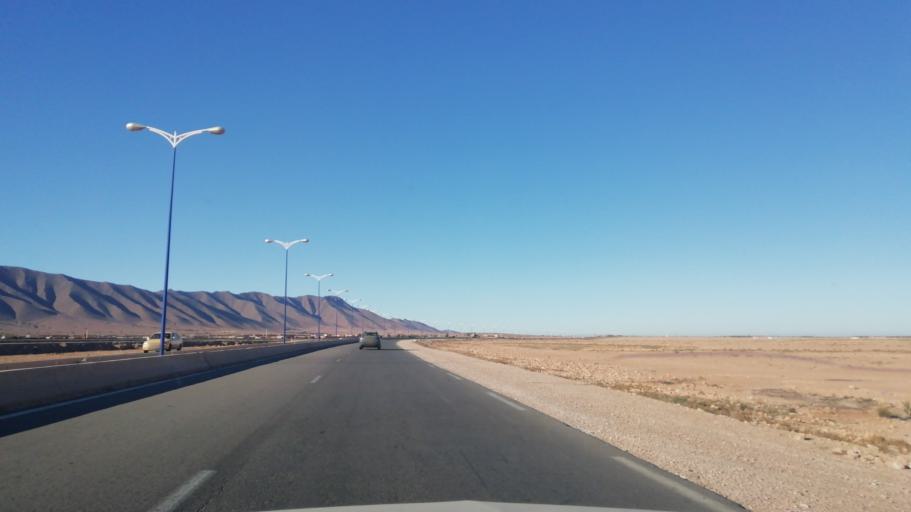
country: DZ
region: Wilaya de Naama
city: Naama
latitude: 33.5660
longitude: -0.2396
